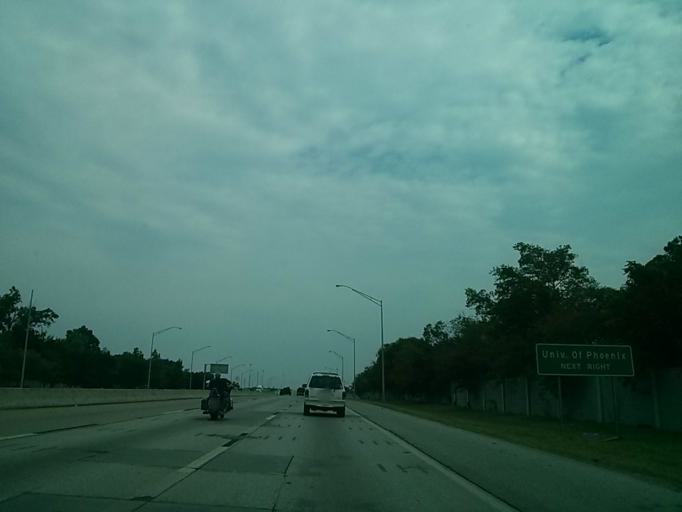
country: US
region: Oklahoma
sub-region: Tulsa County
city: Broken Arrow
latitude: 36.1273
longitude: -95.8595
